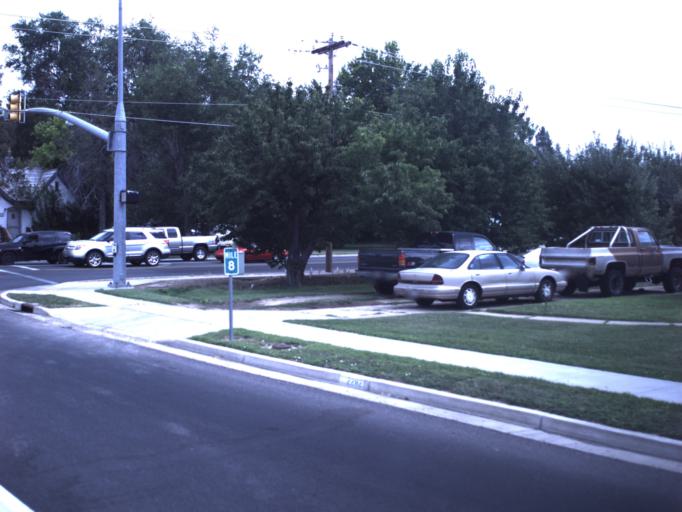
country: US
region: Utah
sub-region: Davis County
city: Clinton
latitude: 41.1468
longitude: -112.0644
